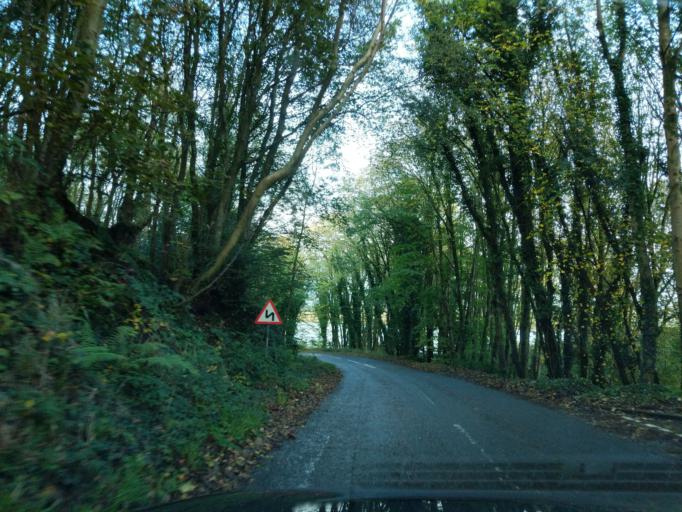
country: GB
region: Scotland
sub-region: Dumfries and Galloway
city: Kirkcudbright
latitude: 54.8131
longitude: -4.0931
